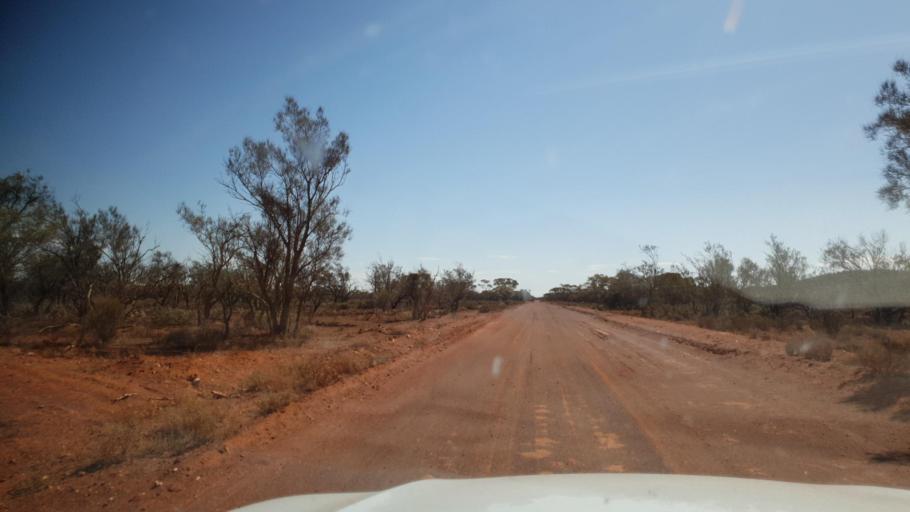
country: AU
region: South Australia
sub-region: Kimba
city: Caralue
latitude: -32.5268
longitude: 136.1725
